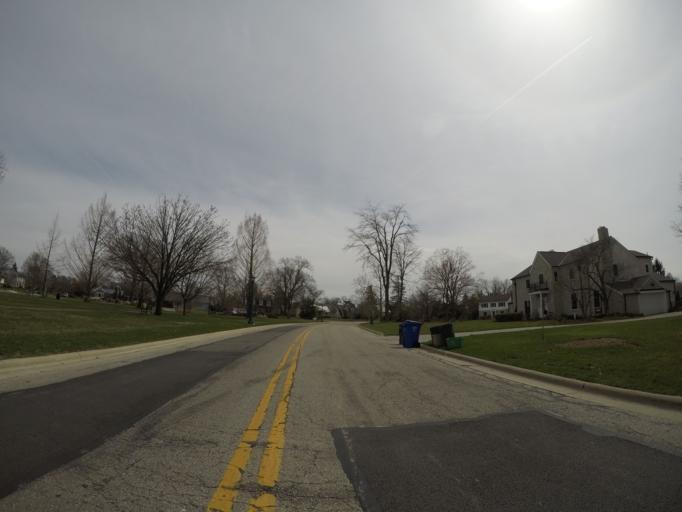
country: US
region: Ohio
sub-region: Franklin County
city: Upper Arlington
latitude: 40.0122
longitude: -83.0711
